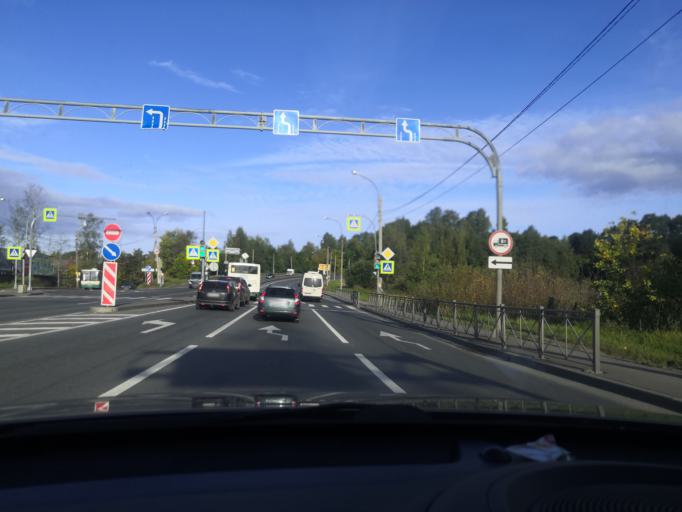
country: RU
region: St.-Petersburg
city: Pargolovo
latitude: 60.0786
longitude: 30.2676
